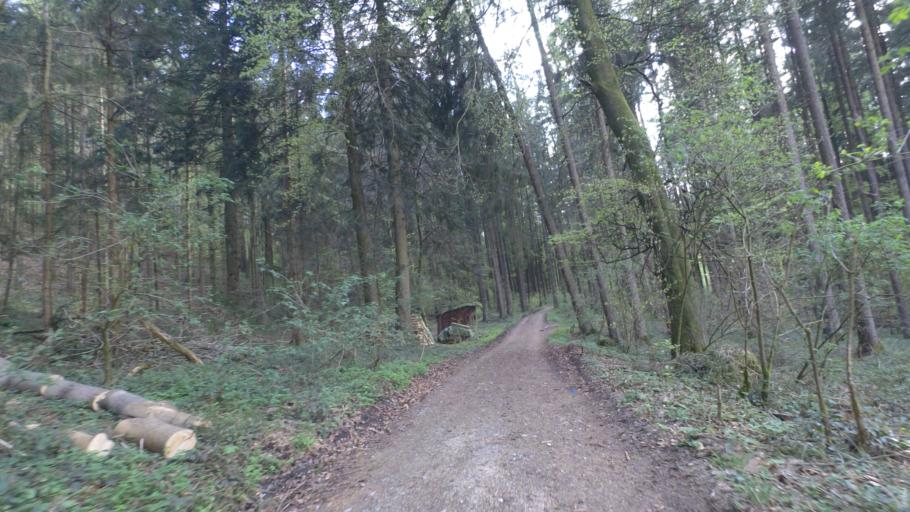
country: DE
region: Bavaria
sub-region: Upper Bavaria
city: Nussdorf
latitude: 47.8989
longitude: 12.5869
